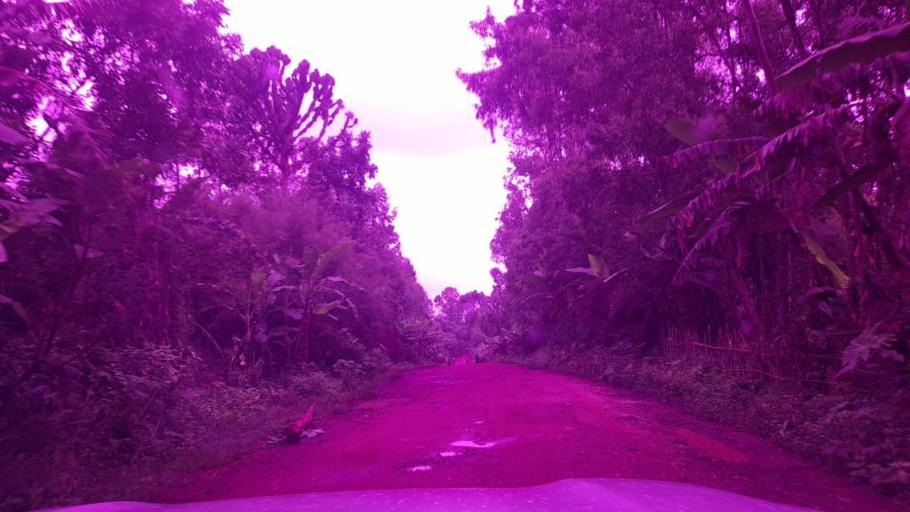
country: ET
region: Southern Nations, Nationalities, and People's Region
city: Bonga
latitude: 7.5836
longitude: 36.0184
